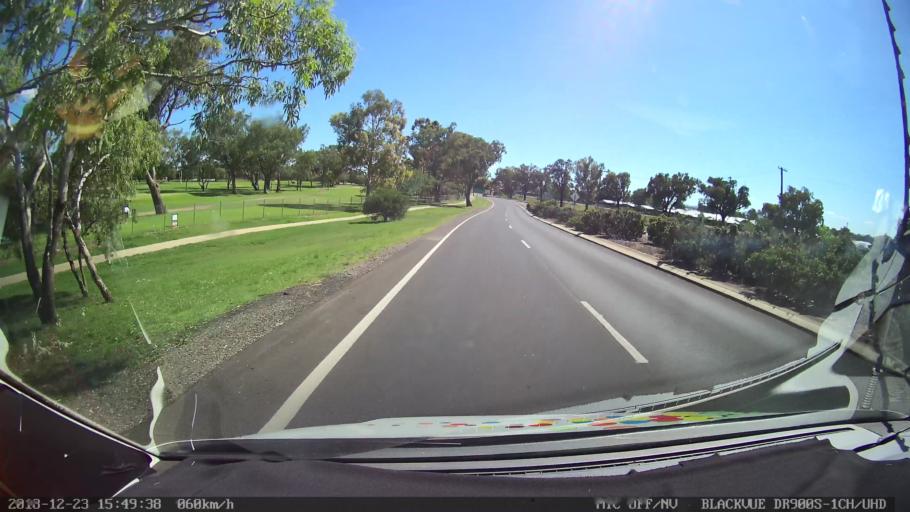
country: AU
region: New South Wales
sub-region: Tamworth Municipality
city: South Tamworth
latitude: -31.1006
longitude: 150.9055
